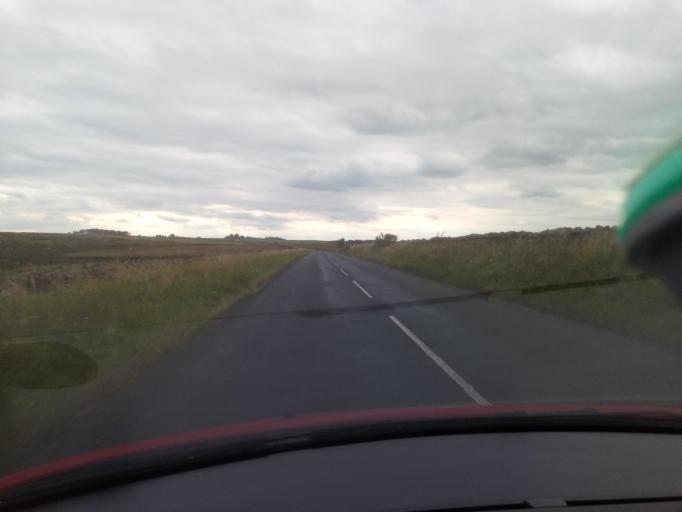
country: GB
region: England
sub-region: Northumberland
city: Warden
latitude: 54.9486
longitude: -2.2193
